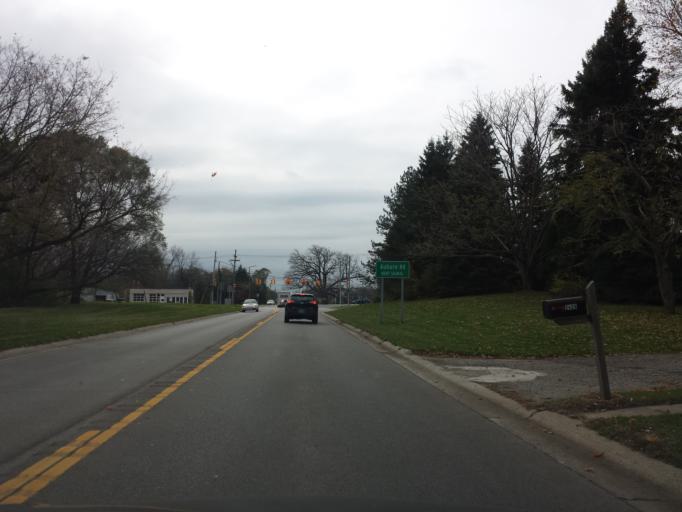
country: US
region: Michigan
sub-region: Oakland County
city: Rochester Hills
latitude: 42.6368
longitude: -83.1521
